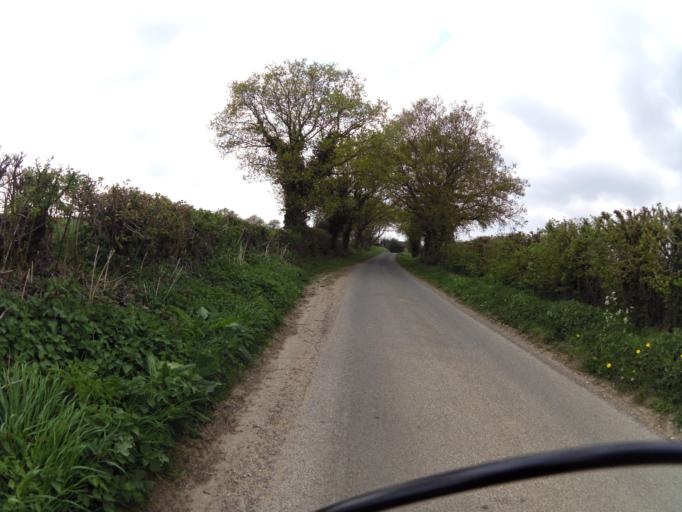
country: GB
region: England
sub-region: Suffolk
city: Hadleigh
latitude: 52.0503
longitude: 0.8961
